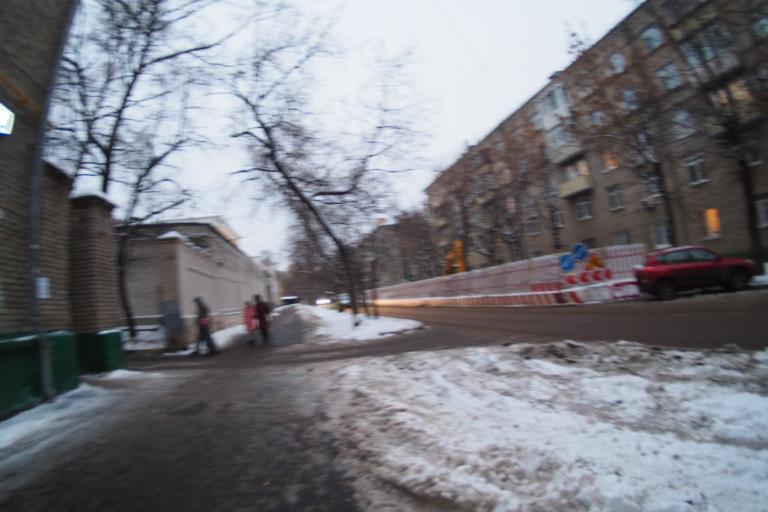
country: RU
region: Moscow
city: Sokol
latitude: 55.7990
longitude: 37.5623
